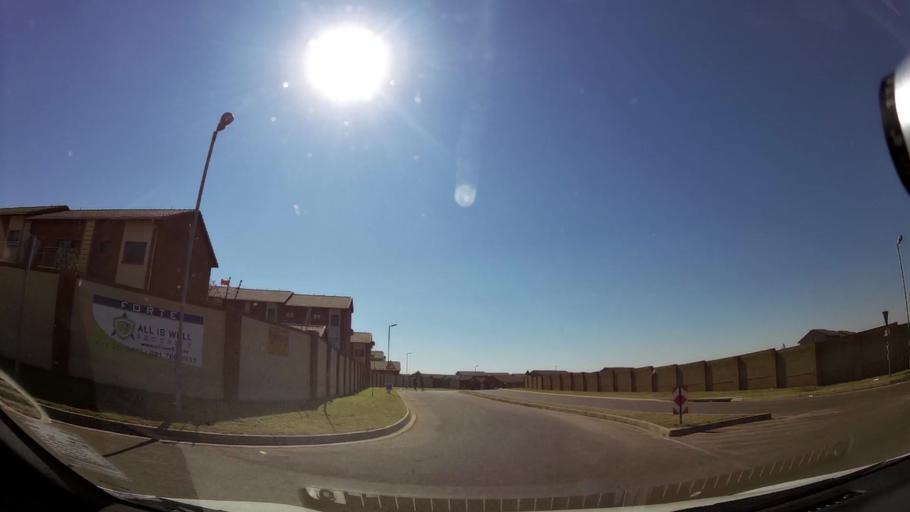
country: ZA
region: Gauteng
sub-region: City of Johannesburg Metropolitan Municipality
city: Midrand
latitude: -25.9492
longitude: 28.1025
